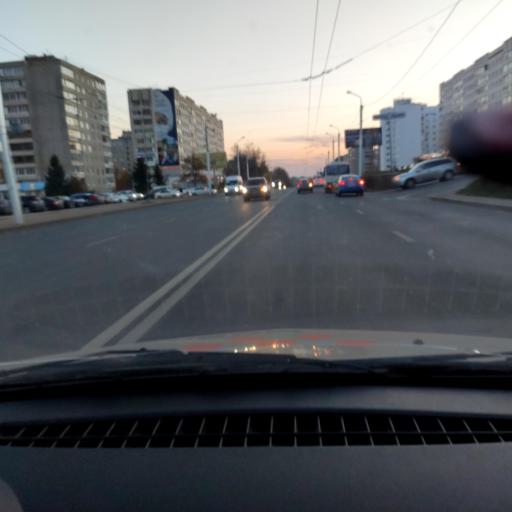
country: RU
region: Bashkortostan
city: Ufa
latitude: 54.7063
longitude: 55.9984
